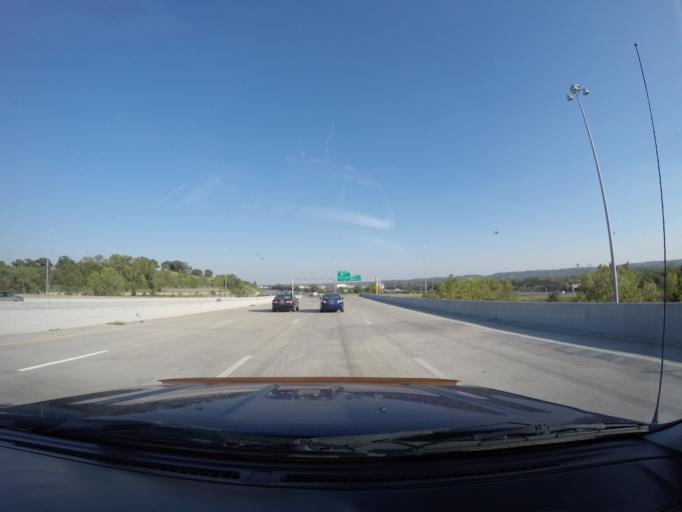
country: US
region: Kansas
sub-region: Wyandotte County
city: Kansas City
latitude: 39.1009
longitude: -94.6711
